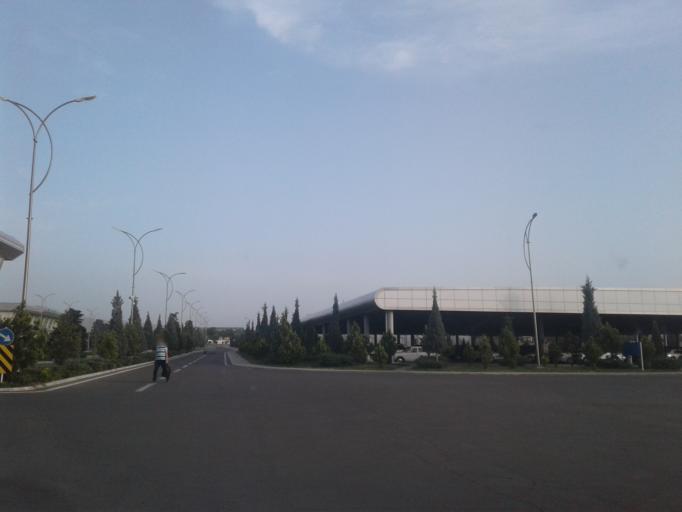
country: TM
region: Balkan
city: Turkmenbasy
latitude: 40.0439
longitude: 52.9931
